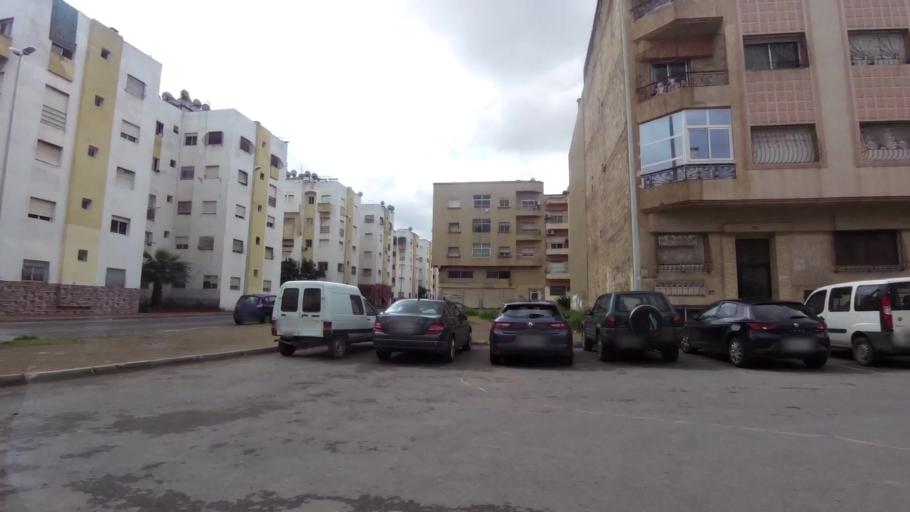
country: MA
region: Grand Casablanca
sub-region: Nouaceur
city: Bouskoura
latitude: 33.5220
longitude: -7.6493
